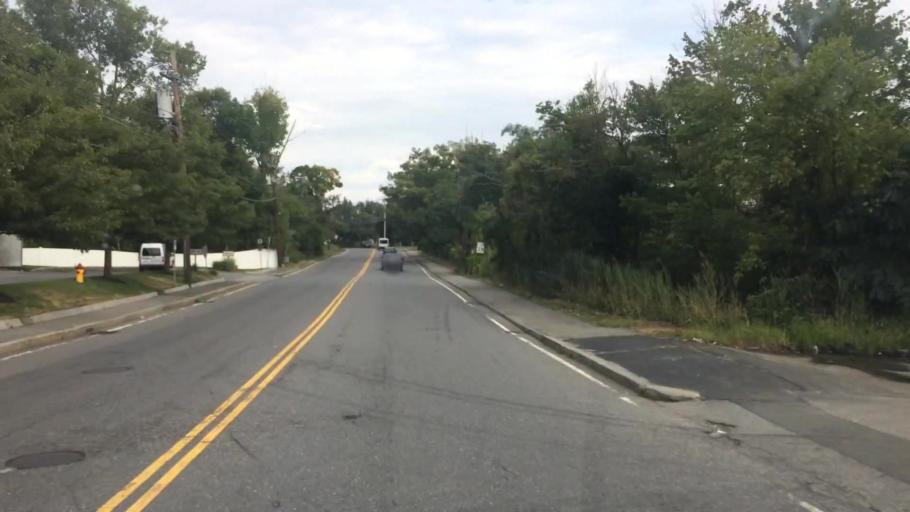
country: US
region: Massachusetts
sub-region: Middlesex County
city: Woburn
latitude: 42.4908
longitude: -71.1736
